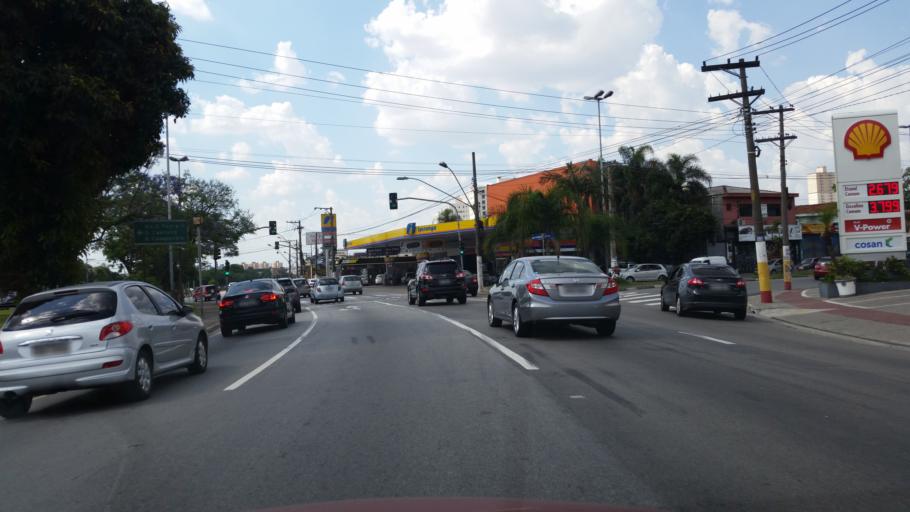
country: BR
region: Sao Paulo
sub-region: Sao Caetano Do Sul
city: Sao Caetano do Sul
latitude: -23.6244
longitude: -46.5410
